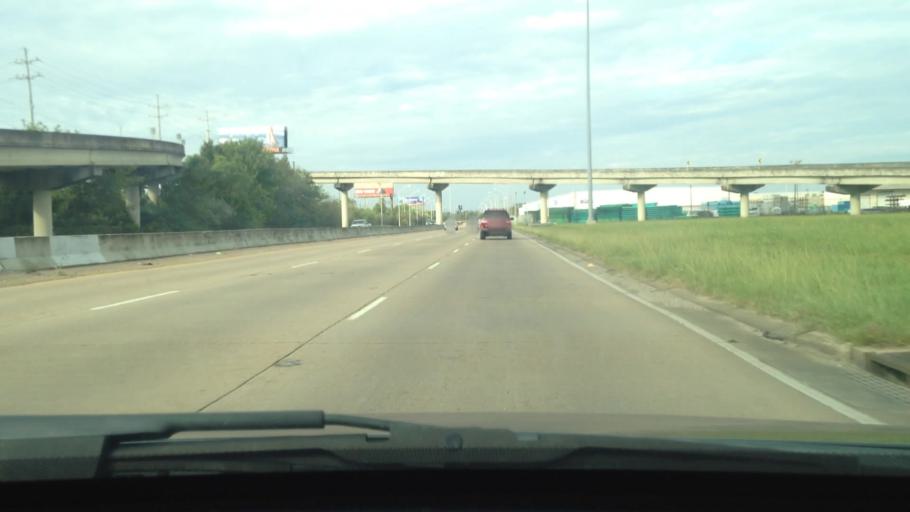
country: US
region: Louisiana
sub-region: Jefferson Parish
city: Jefferson
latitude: 29.9700
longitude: -90.1434
